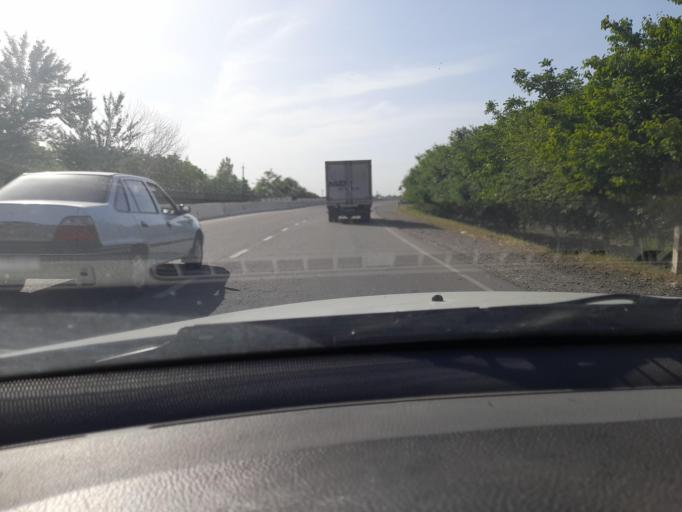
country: UZ
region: Samarqand
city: Kattaqo'rg'on
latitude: 39.9243
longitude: 66.2758
